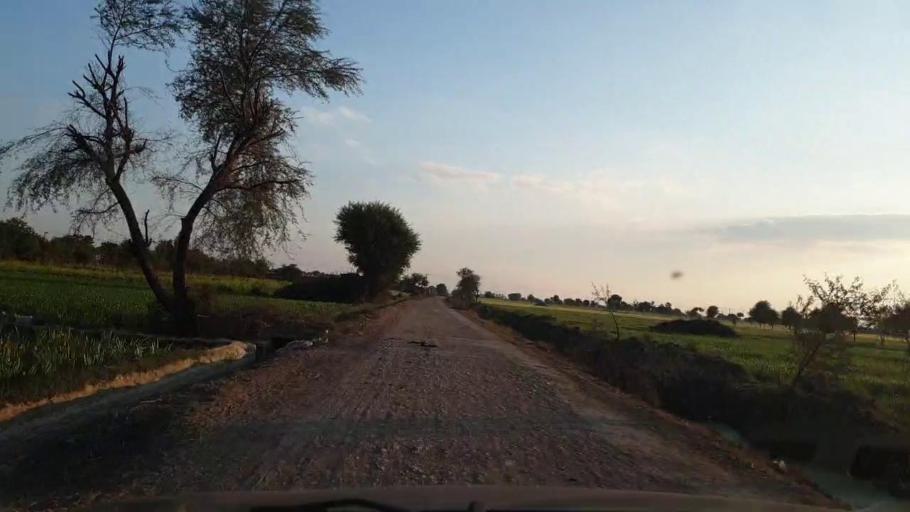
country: PK
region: Sindh
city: Sinjhoro
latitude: 26.0003
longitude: 68.8014
